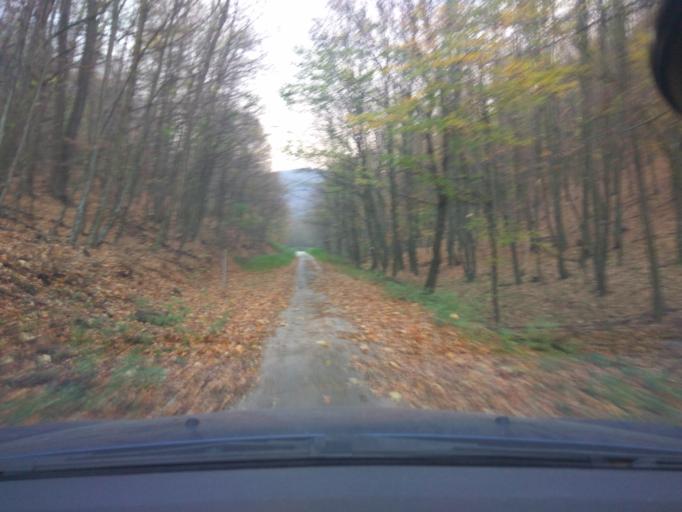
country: SK
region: Trnavsky
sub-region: Okres Trnava
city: Piestany
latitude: 48.6020
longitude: 17.9495
